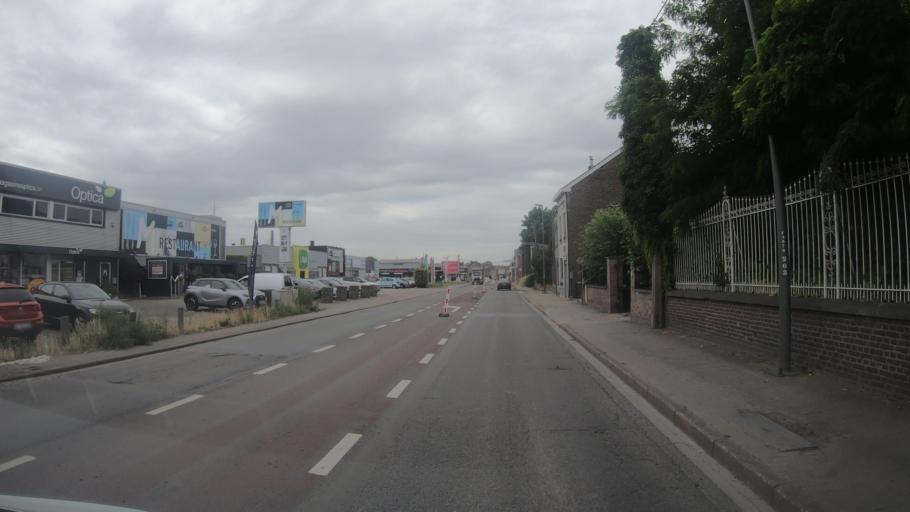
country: BE
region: Wallonia
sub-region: Province de Liege
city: Herstal
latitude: 50.6815
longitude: 5.6419
